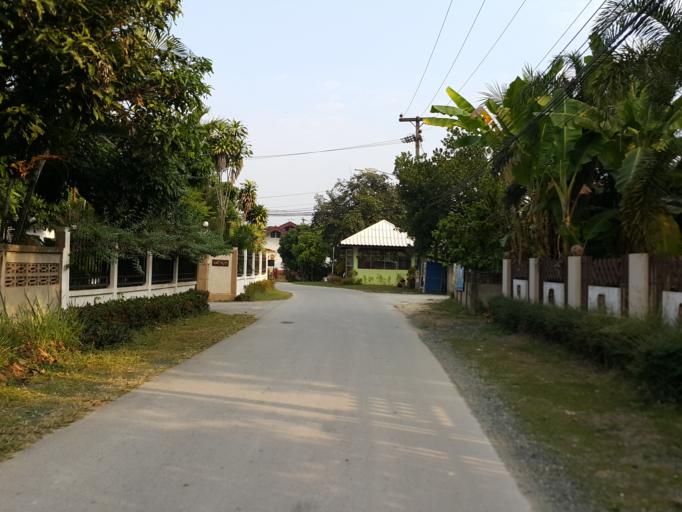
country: TH
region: Chiang Mai
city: San Sai
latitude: 18.8244
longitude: 99.1051
